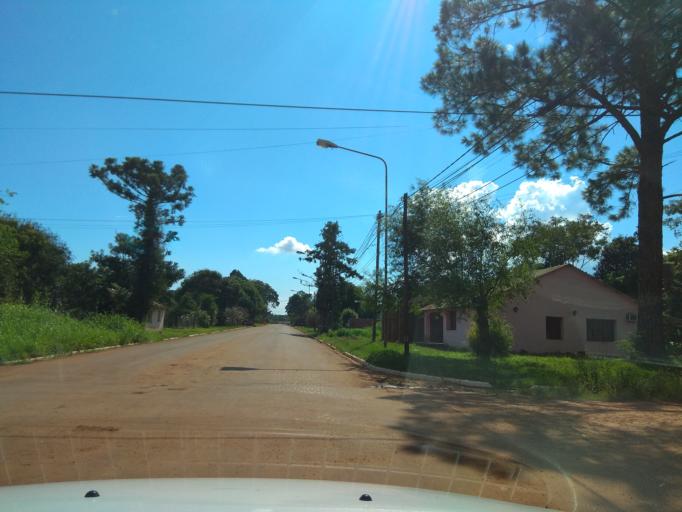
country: AR
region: Misiones
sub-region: Departamento de Candelaria
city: Candelaria
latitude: -27.4600
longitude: -55.7508
